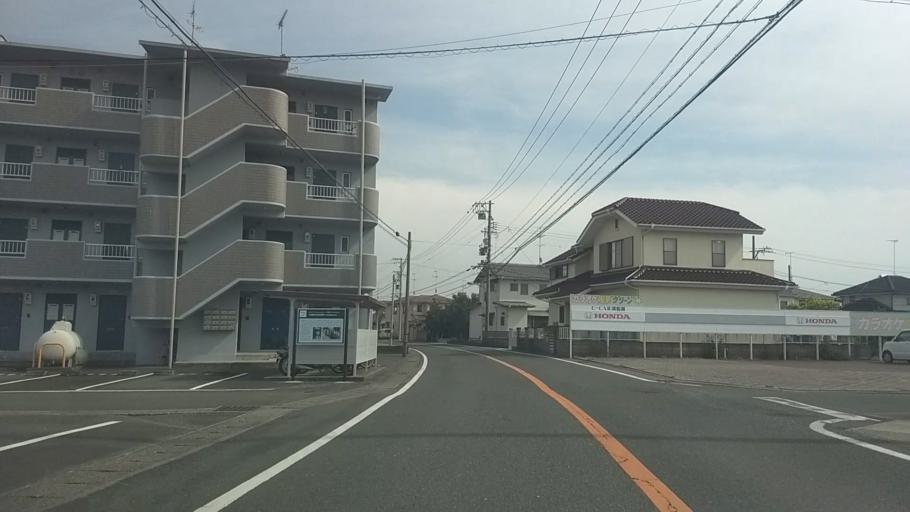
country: JP
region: Shizuoka
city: Kosai-shi
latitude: 34.7121
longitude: 137.6203
